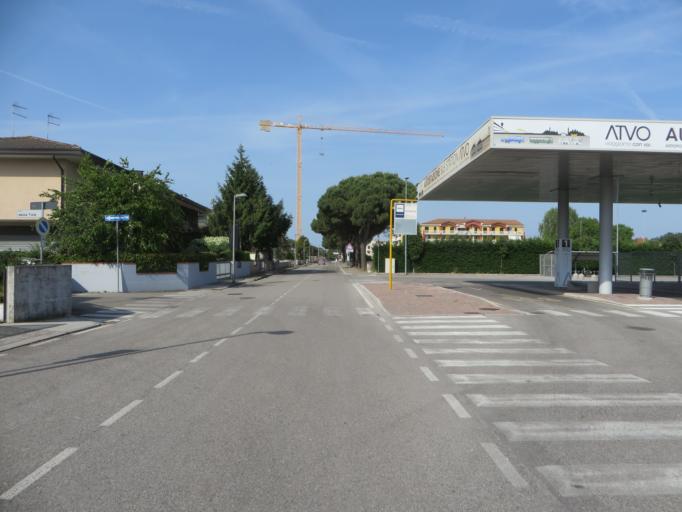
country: IT
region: Veneto
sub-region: Provincia di Venezia
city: Crepaldo
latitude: 45.5479
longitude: 12.7578
